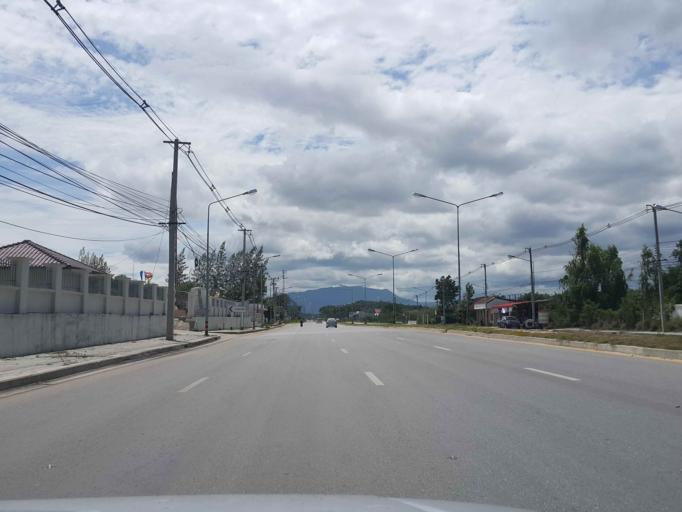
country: TH
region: Tak
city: Tak
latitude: 16.8858
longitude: 99.1920
